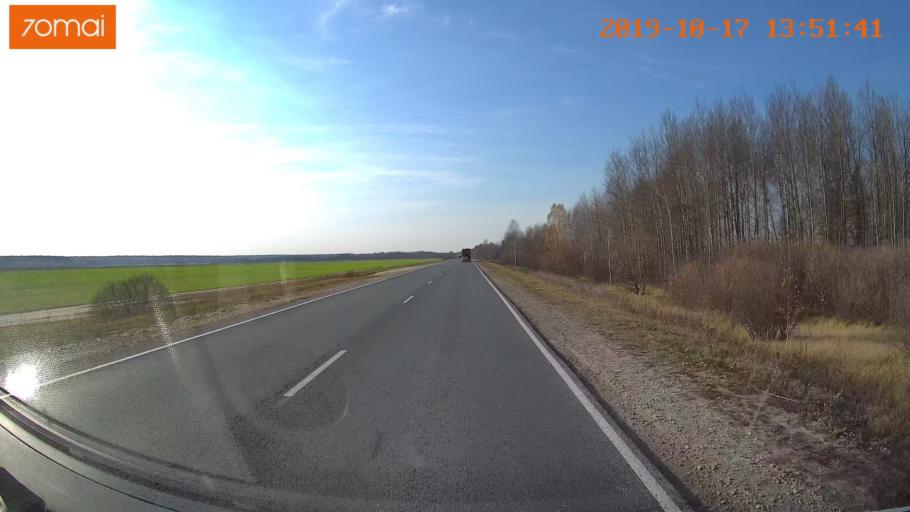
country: RU
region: Rjazan
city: Tuma
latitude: 55.1399
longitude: 40.3824
